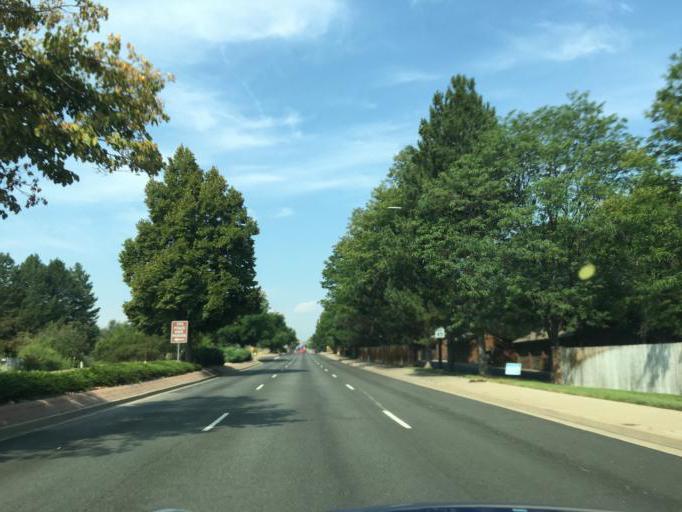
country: US
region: Colorado
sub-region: Jefferson County
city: Arvada
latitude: 39.8419
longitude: -105.1003
